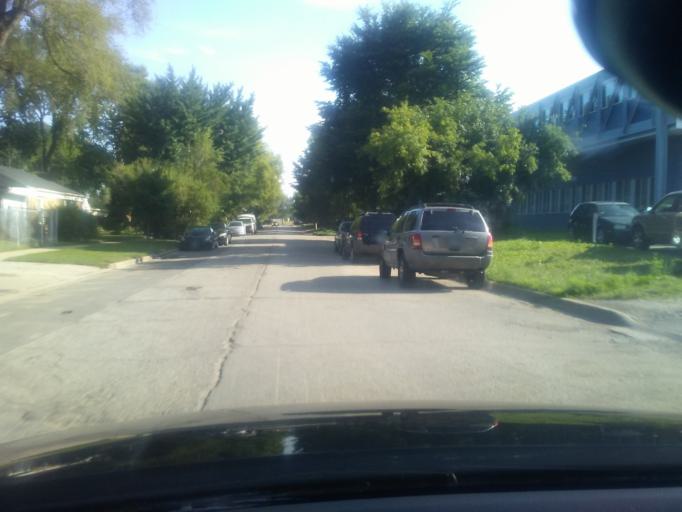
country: US
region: Illinois
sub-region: Cook County
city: Evanston
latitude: 42.0288
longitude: -87.7041
